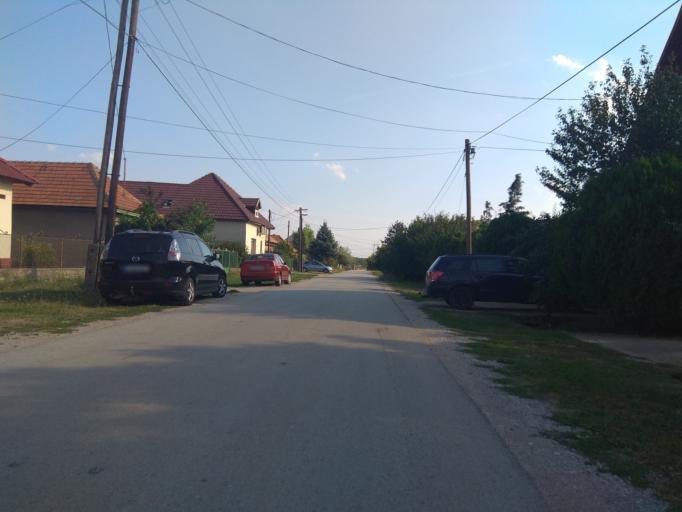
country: HU
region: Borsod-Abauj-Zemplen
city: Mezokeresztes
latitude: 47.8815
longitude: 20.6851
